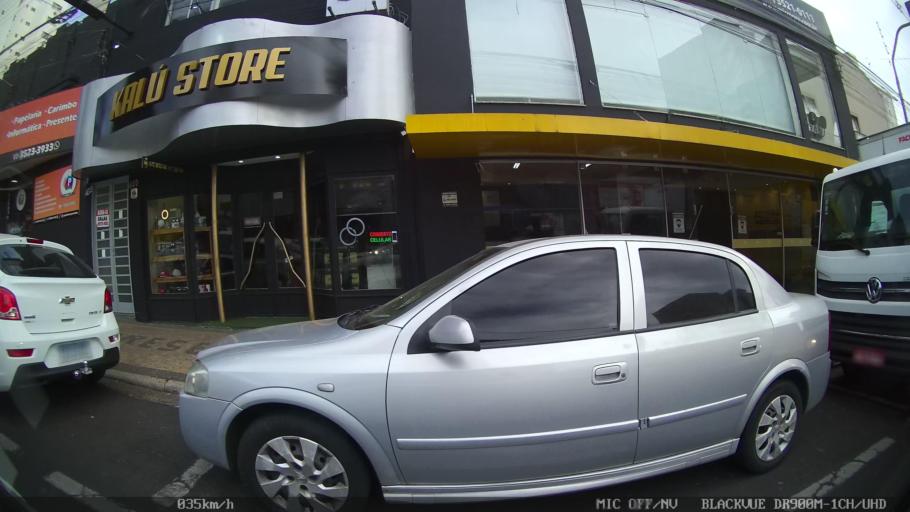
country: BR
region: Sao Paulo
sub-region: Catanduva
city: Catanduva
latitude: -21.1347
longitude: -48.9729
